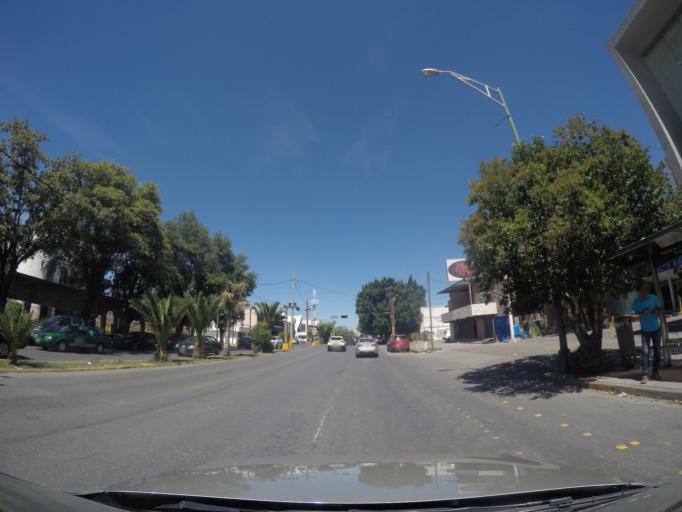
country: MX
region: San Luis Potosi
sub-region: San Luis Potosi
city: San Luis Potosi
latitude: 22.1490
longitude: -101.0071
